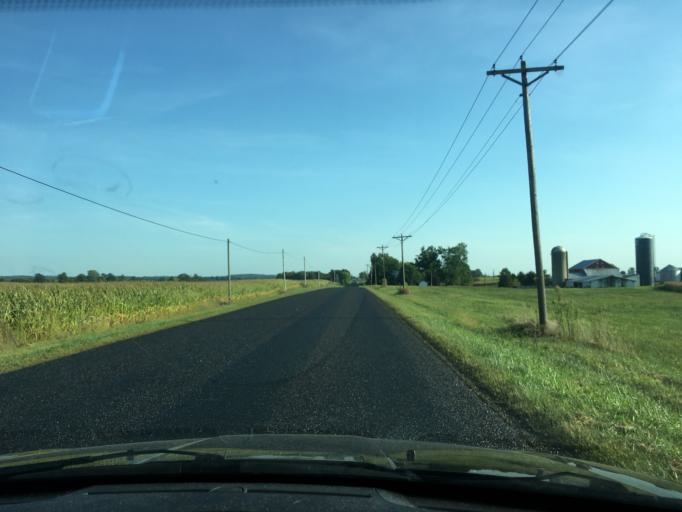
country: US
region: Ohio
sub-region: Logan County
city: West Liberty
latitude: 40.2981
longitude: -83.7318
